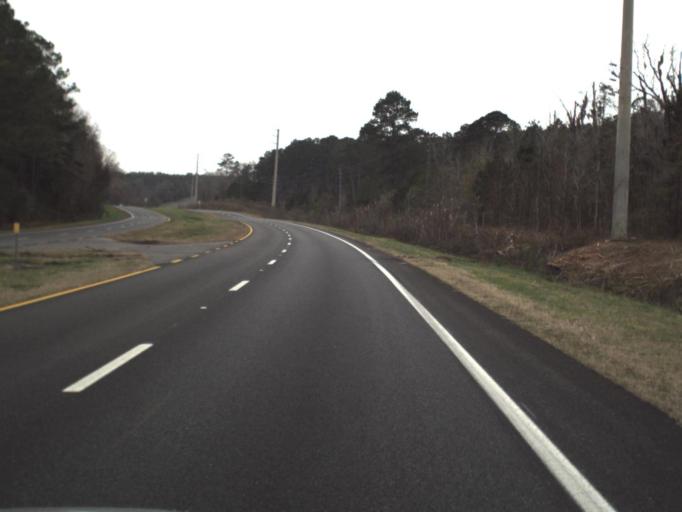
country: US
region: Florida
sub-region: Jefferson County
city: Monticello
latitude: 30.4120
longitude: -83.9155
